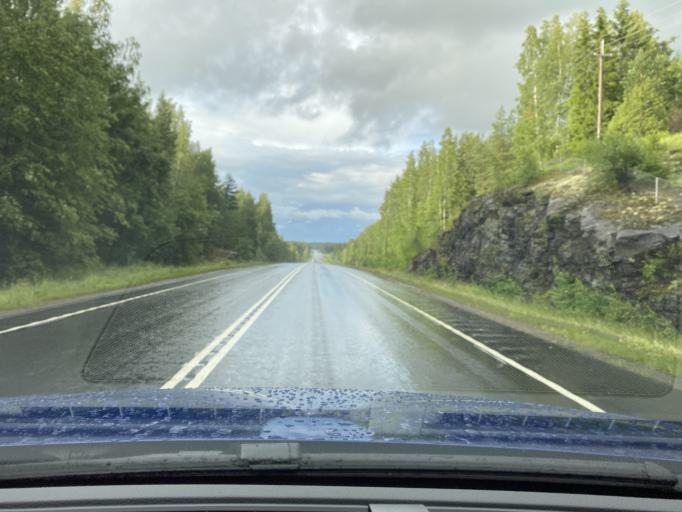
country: FI
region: Uusimaa
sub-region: Helsinki
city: Nurmijaervi
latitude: 60.4640
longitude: 24.8353
